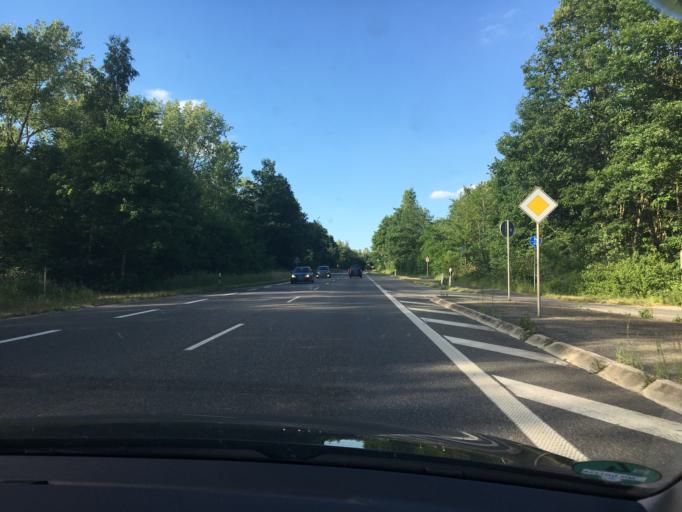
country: DE
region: North Rhine-Westphalia
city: Tuernich
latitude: 50.8747
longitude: 6.7749
